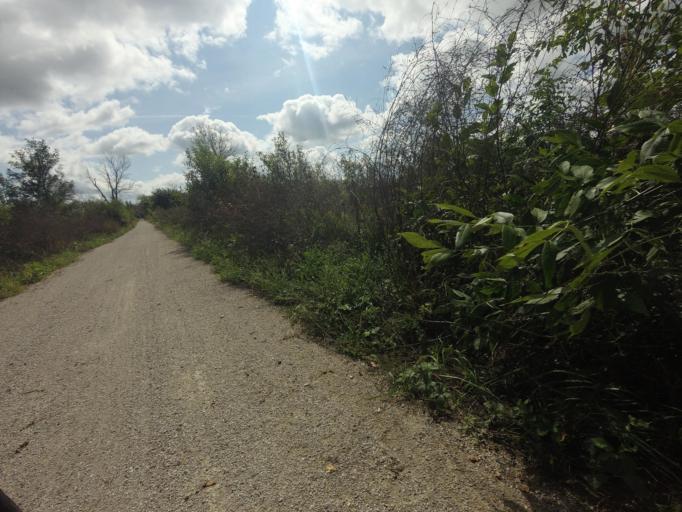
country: CA
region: Ontario
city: Huron East
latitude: 43.6207
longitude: -81.1551
